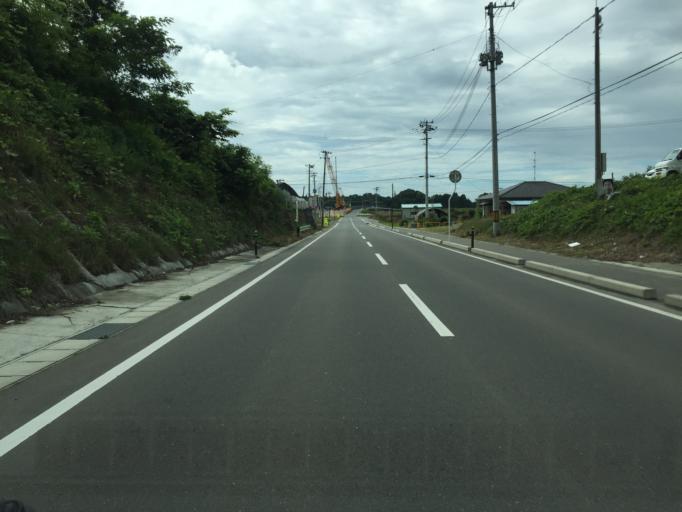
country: JP
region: Miyagi
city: Marumori
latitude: 37.8119
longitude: 140.9545
